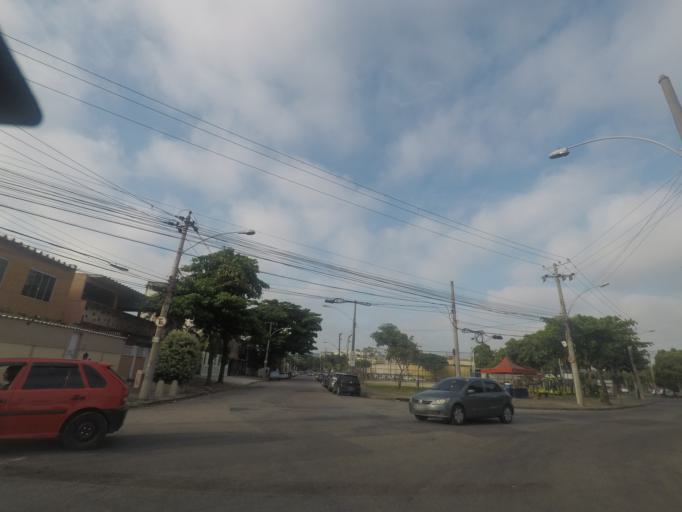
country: BR
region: Rio de Janeiro
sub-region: Duque De Caxias
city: Duque de Caxias
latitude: -22.8366
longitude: -43.2634
